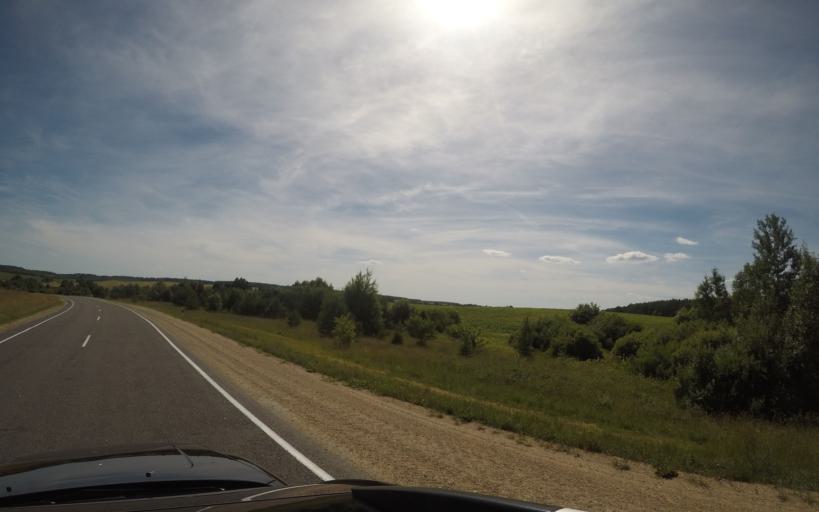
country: BY
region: Grodnenskaya
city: Hal'shany
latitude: 54.2644
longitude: 25.9875
